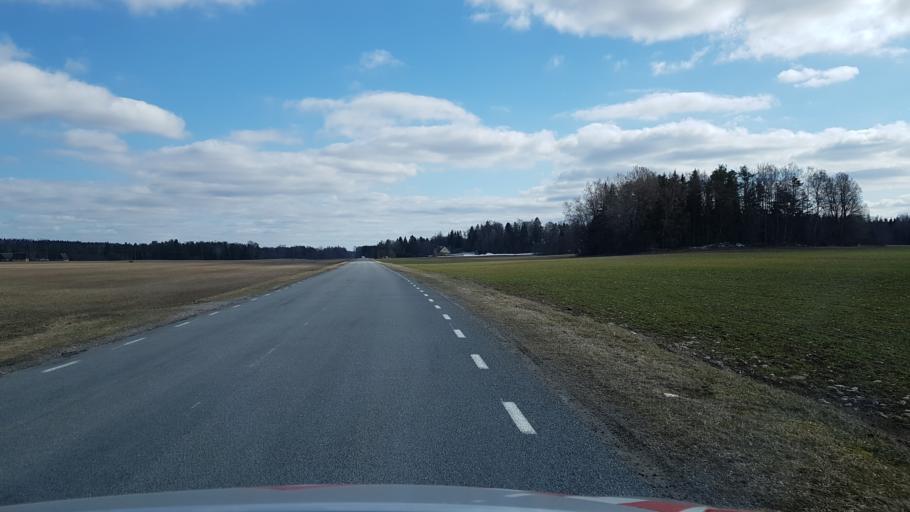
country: EE
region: Laeaene-Virumaa
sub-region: Tamsalu vald
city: Tamsalu
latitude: 59.1749
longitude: 26.0543
